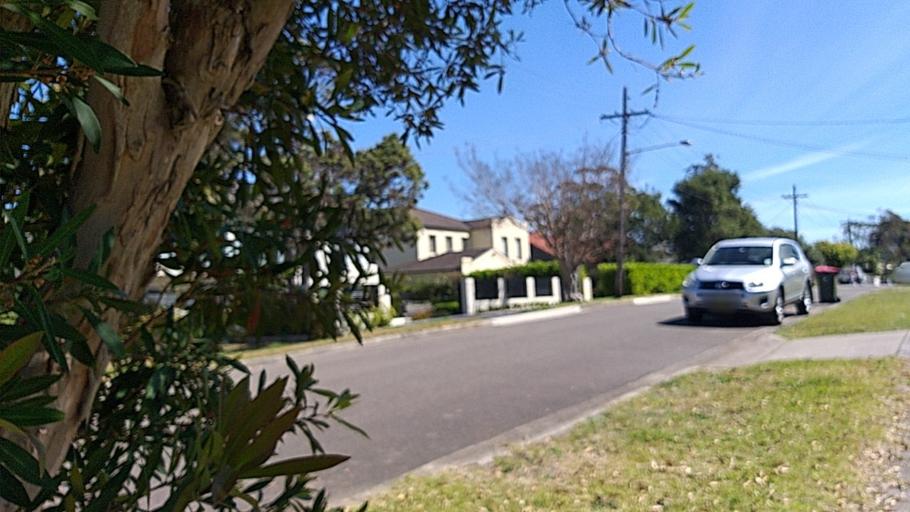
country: AU
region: New South Wales
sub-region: Hunters Hill
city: Gladesville
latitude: -33.8258
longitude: 151.1217
